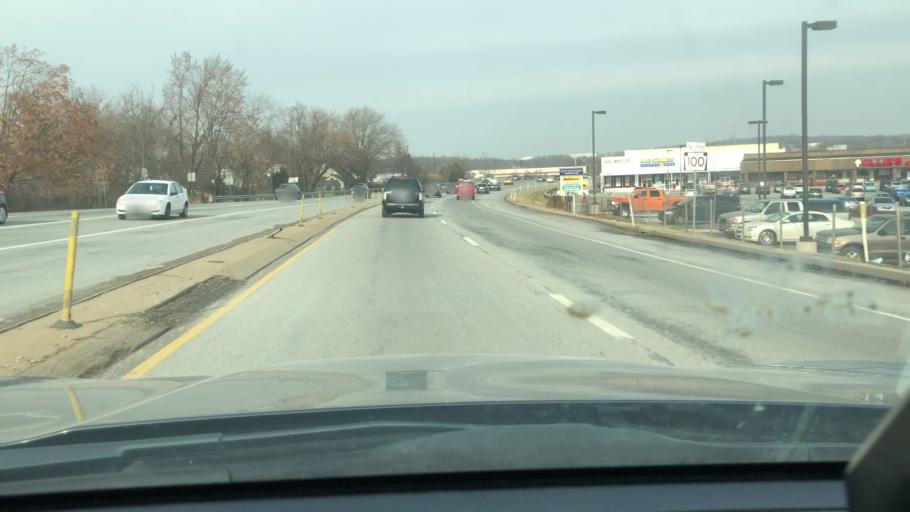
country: US
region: Pennsylvania
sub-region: Montgomery County
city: Pottstown
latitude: 40.2496
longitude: -75.6614
